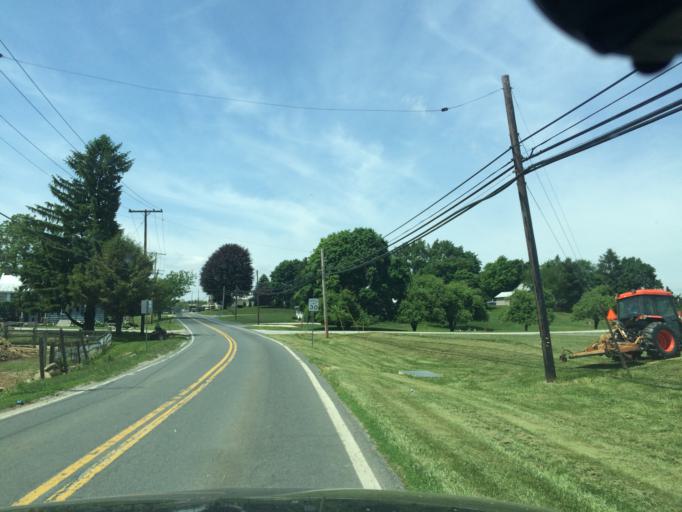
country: US
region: Maryland
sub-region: Carroll County
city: Westminster
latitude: 39.5412
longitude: -76.9356
